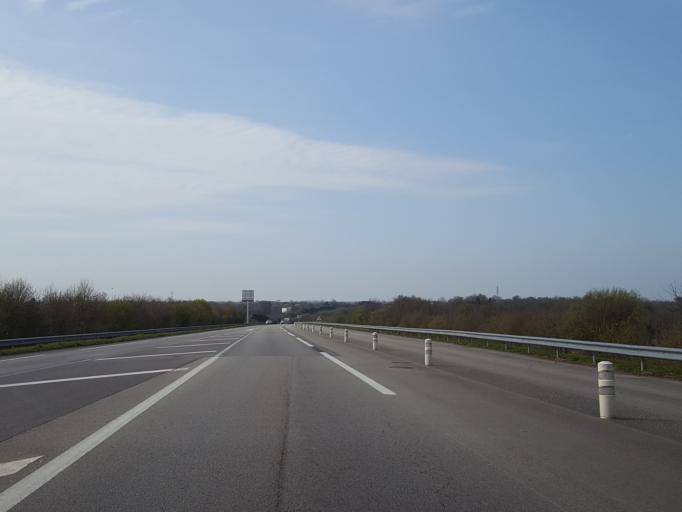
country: FR
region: Pays de la Loire
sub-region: Departement de la Vendee
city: La Roche-sur-Yon
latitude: 46.6767
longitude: -1.4543
